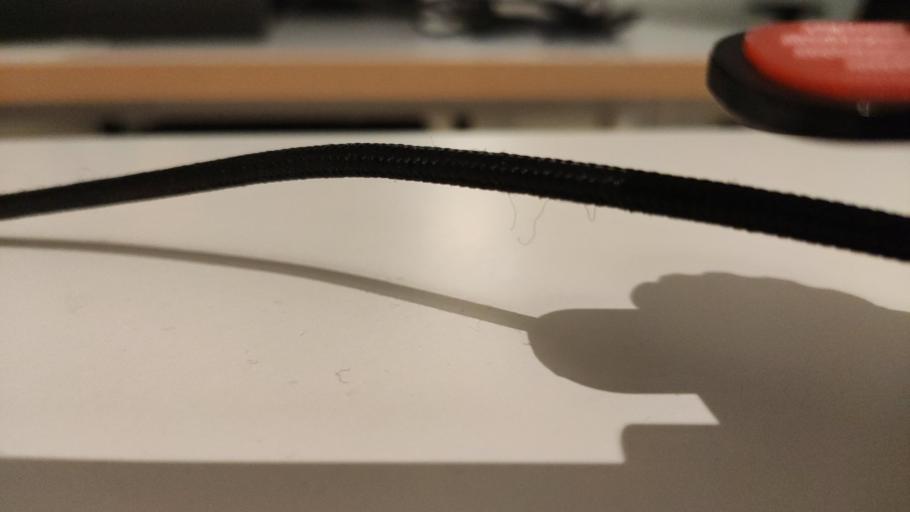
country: RU
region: Moskovskaya
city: Rogachevo
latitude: 56.4055
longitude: 37.2430
